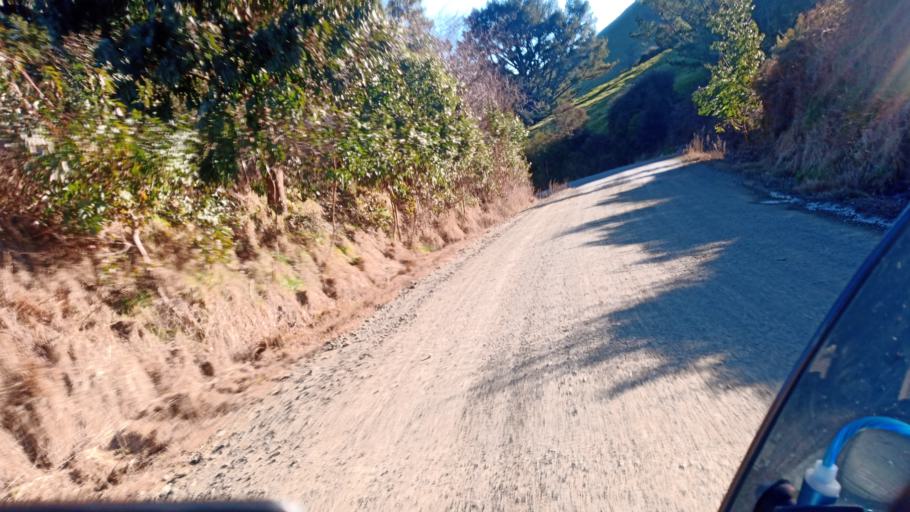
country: NZ
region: Bay of Plenty
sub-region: Opotiki District
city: Opotiki
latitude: -38.4607
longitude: 177.4244
